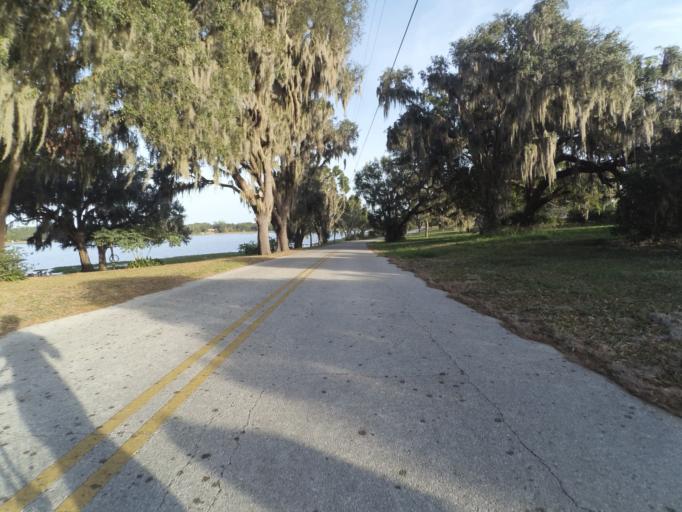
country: US
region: Florida
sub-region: Lake County
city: Umatilla
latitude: 28.9394
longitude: -81.6569
